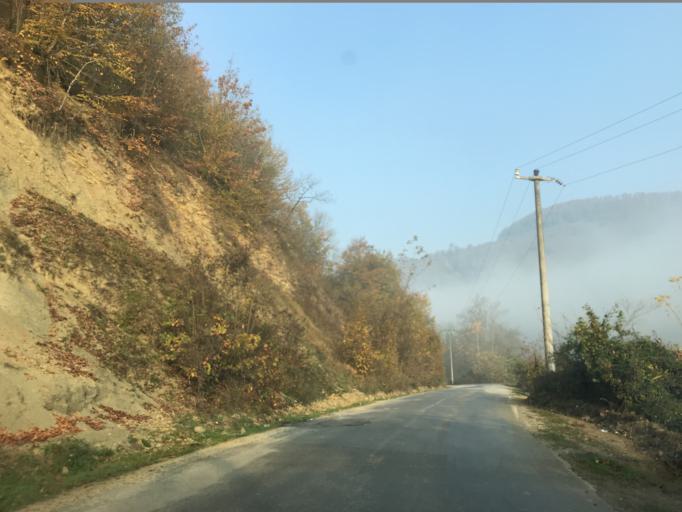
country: TR
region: Duzce
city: Cumayeri
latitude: 40.9108
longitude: 30.9447
